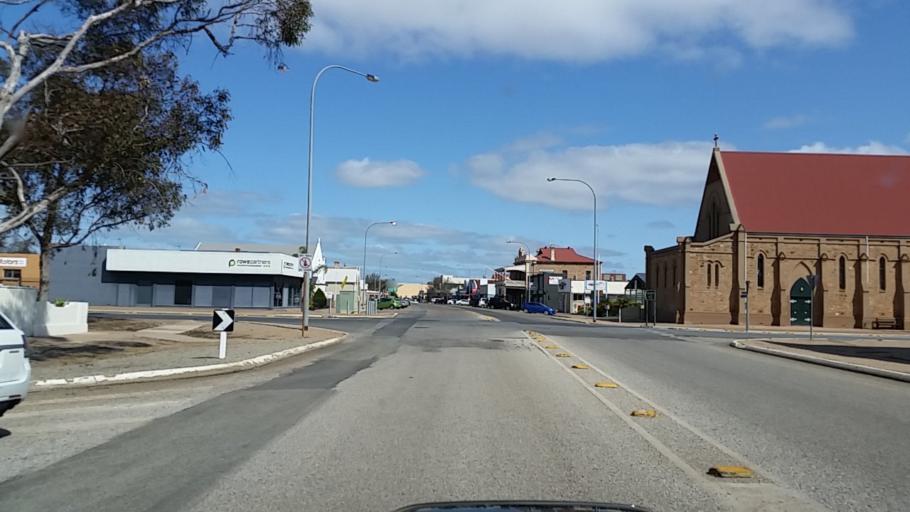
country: AU
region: South Australia
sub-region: Port Pirie City and Dists
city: Port Pirie
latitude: -33.1750
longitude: 138.0084
